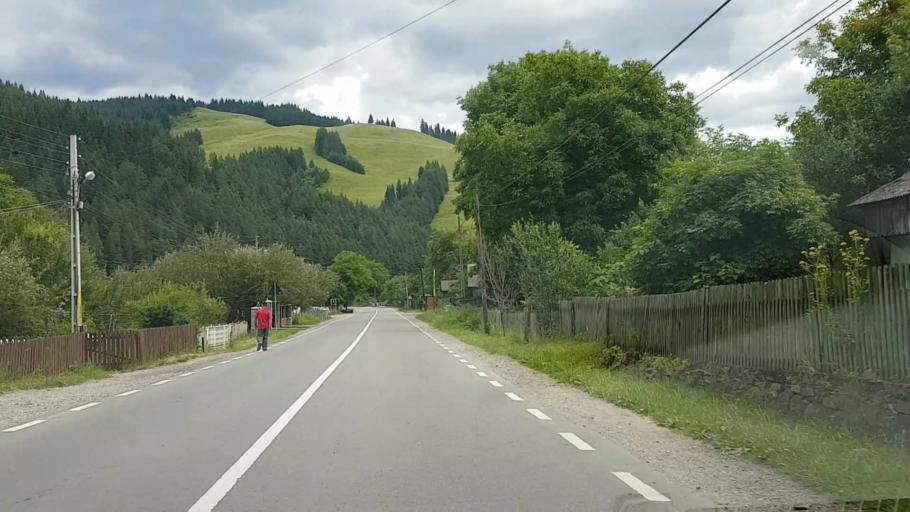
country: RO
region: Neamt
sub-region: Comuna Farcasa
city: Farcasa
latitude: 47.1354
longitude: 25.8911
